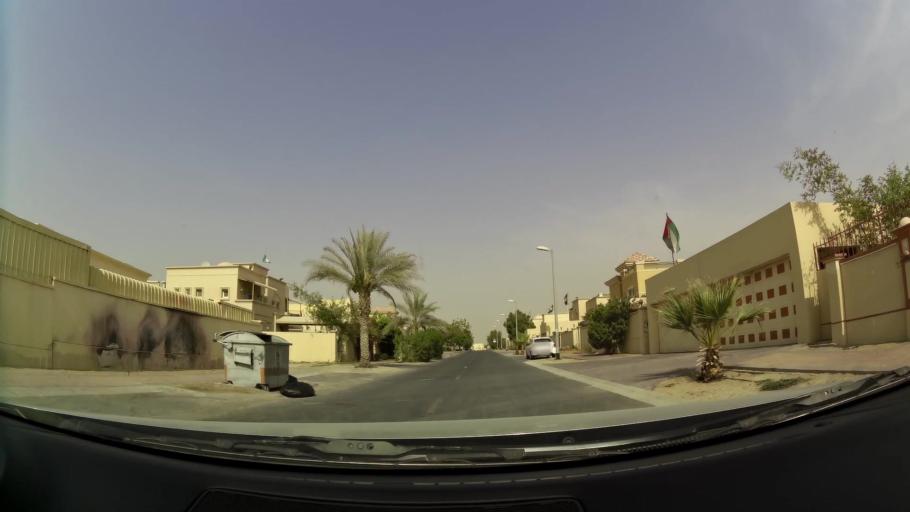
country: AE
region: Ash Shariqah
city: Sharjah
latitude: 25.2622
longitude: 55.4511
